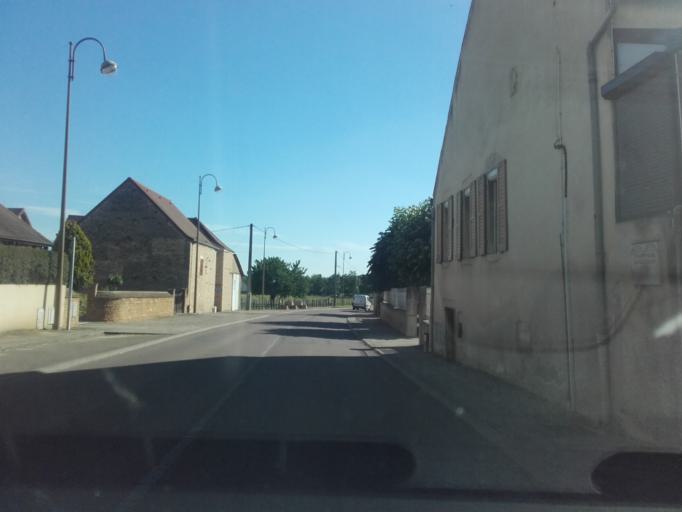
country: FR
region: Bourgogne
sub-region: Departement de la Cote-d'Or
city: Bligny-les-Beaune
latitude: 46.9848
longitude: 4.8235
